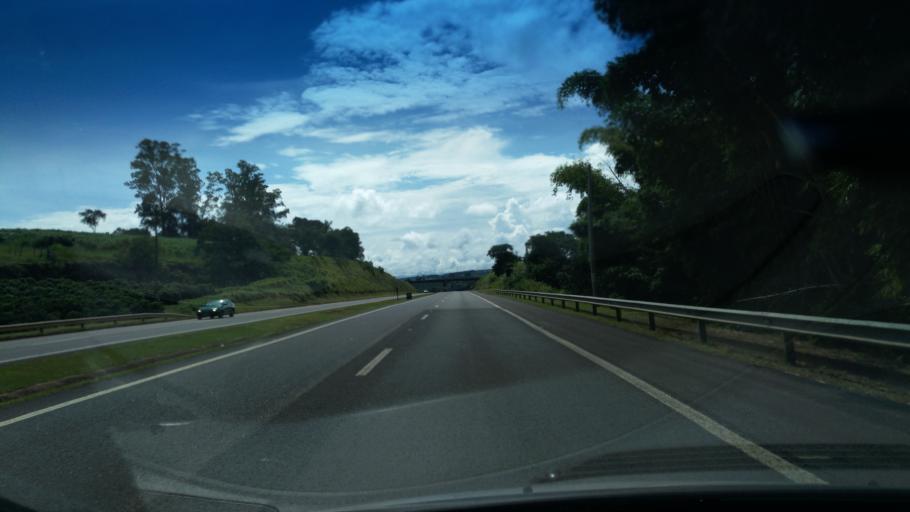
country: BR
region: Sao Paulo
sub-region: Santo Antonio Do Jardim
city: Espirito Santo do Pinhal
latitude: -22.2430
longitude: -46.8040
